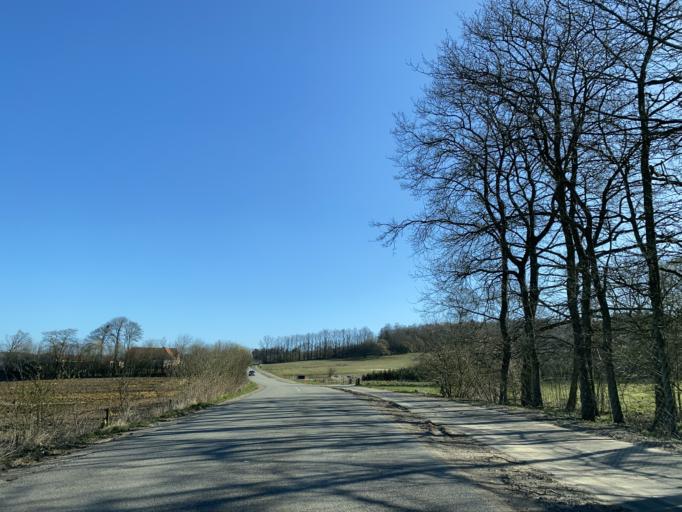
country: DK
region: Central Jutland
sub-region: Favrskov Kommune
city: Ulstrup
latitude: 56.3789
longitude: 9.7390
